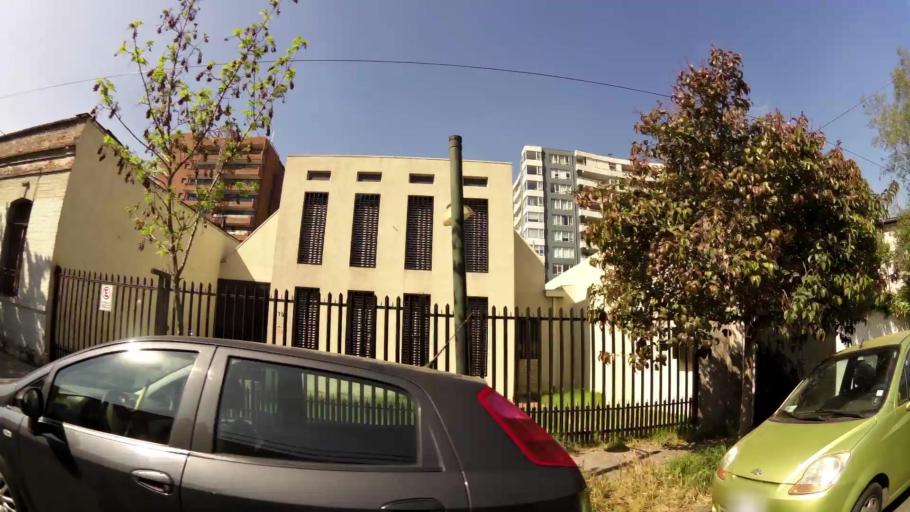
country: CL
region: Santiago Metropolitan
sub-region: Provincia de Santiago
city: Santiago
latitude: -33.4499
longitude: -70.6232
